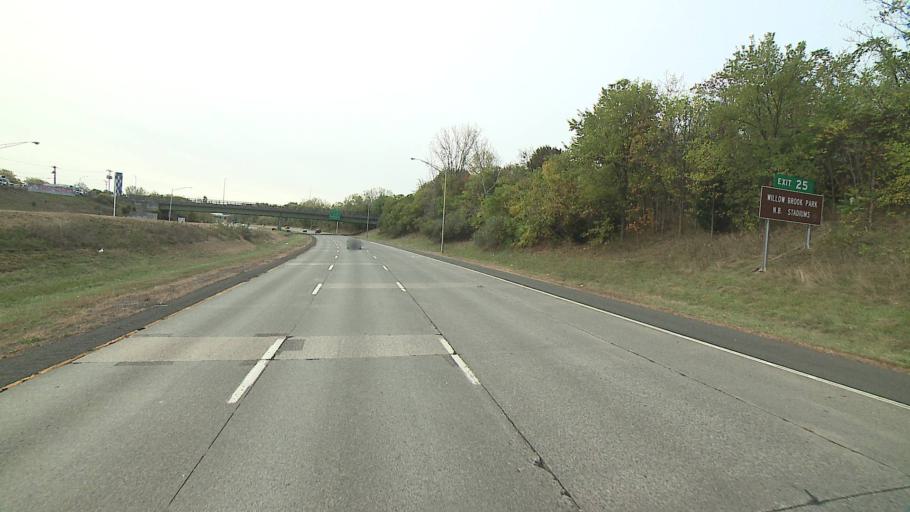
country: US
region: Connecticut
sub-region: Hartford County
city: New Britain
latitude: 41.6634
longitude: -72.7745
